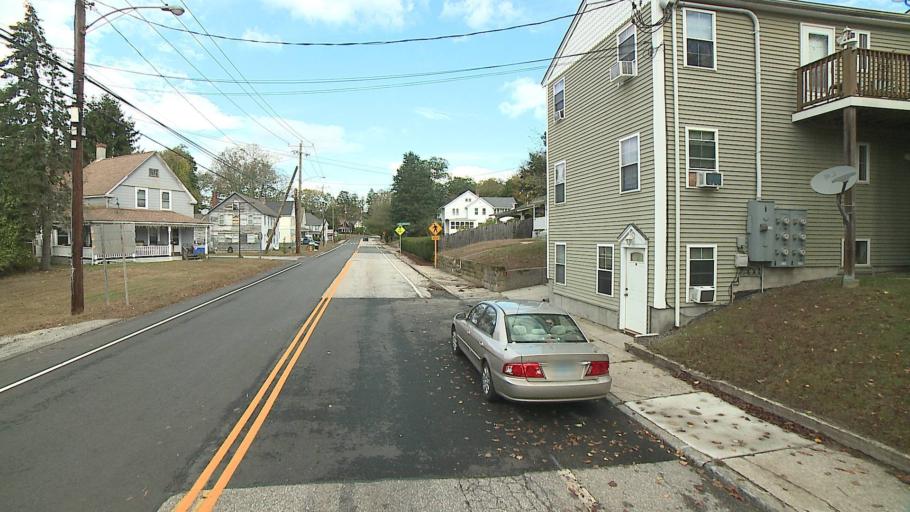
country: US
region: Connecticut
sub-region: Windham County
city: Putnam
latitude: 41.9238
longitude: -71.8996
